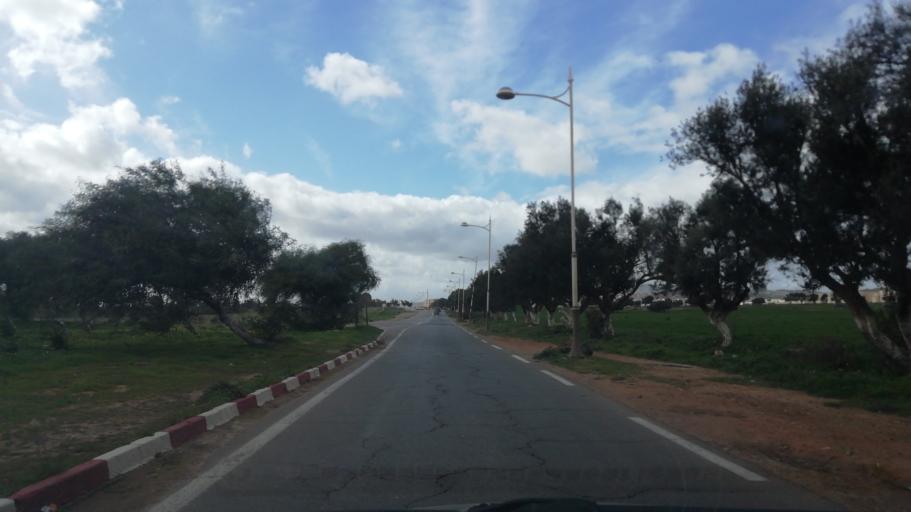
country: DZ
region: Oran
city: Ain el Bya
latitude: 35.7889
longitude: -0.4090
